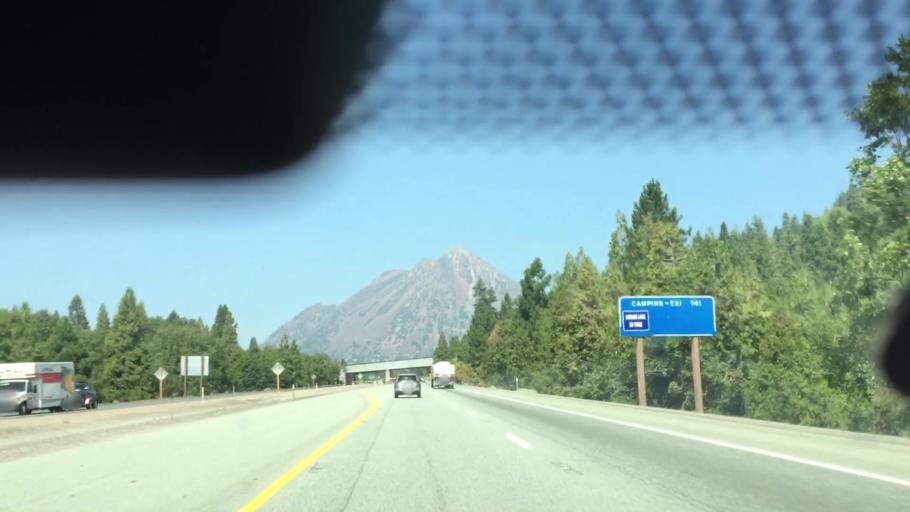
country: US
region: California
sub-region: Siskiyou County
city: Mount Shasta
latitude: 41.3250
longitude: -122.3305
